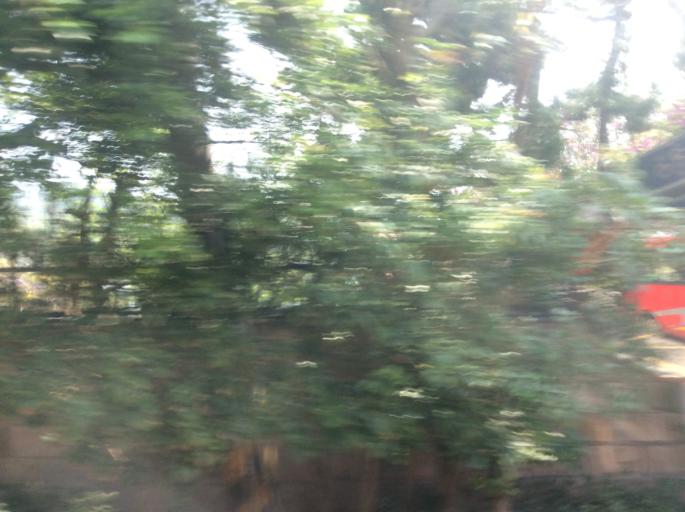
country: TW
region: Taipei
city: Taipei
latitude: 25.1227
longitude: 121.5518
